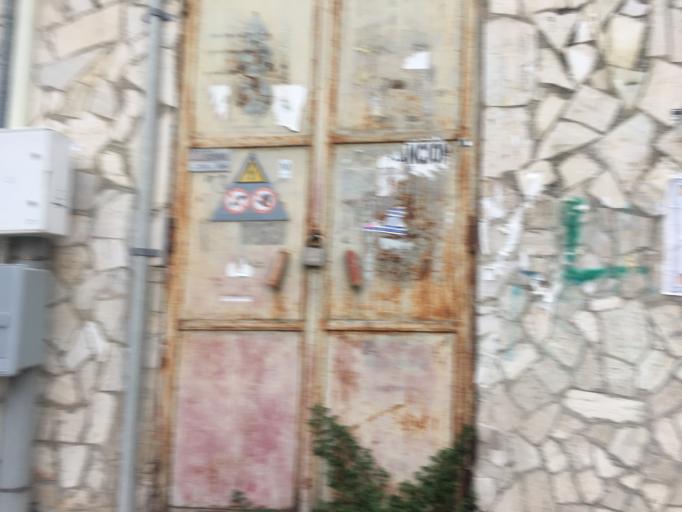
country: IT
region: Campania
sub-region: Provincia di Napoli
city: Napoli
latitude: 40.8590
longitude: 14.2213
